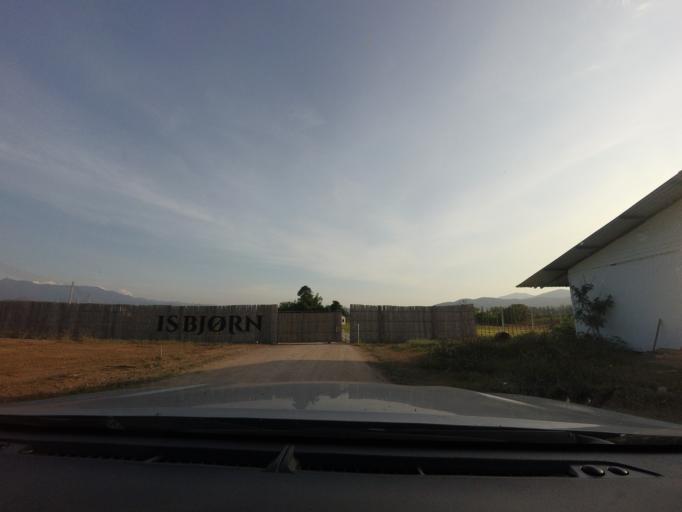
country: TH
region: Chiang Mai
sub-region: Amphoe Chiang Dao
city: Chiang Dao
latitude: 19.3351
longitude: 98.9609
